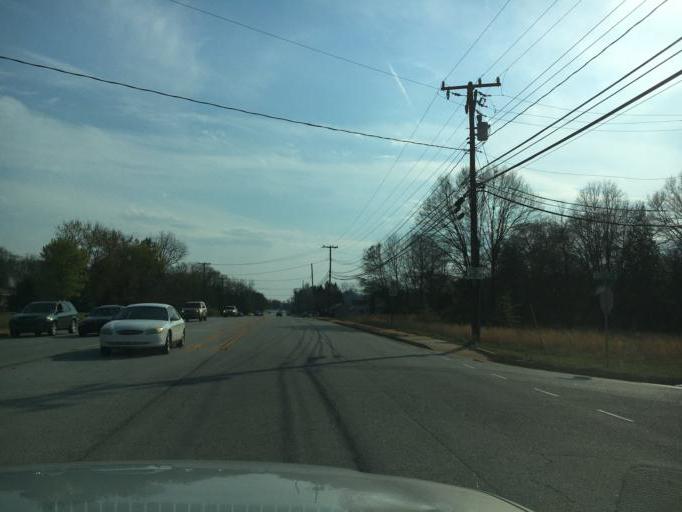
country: US
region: South Carolina
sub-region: Spartanburg County
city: Spartanburg
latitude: 35.0051
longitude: -81.9073
